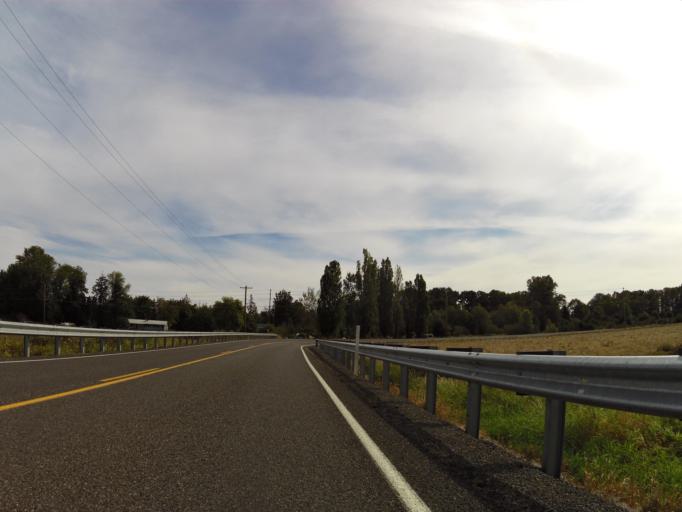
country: US
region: Washington
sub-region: Lewis County
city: Chehalis
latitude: 46.6413
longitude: -122.9737
